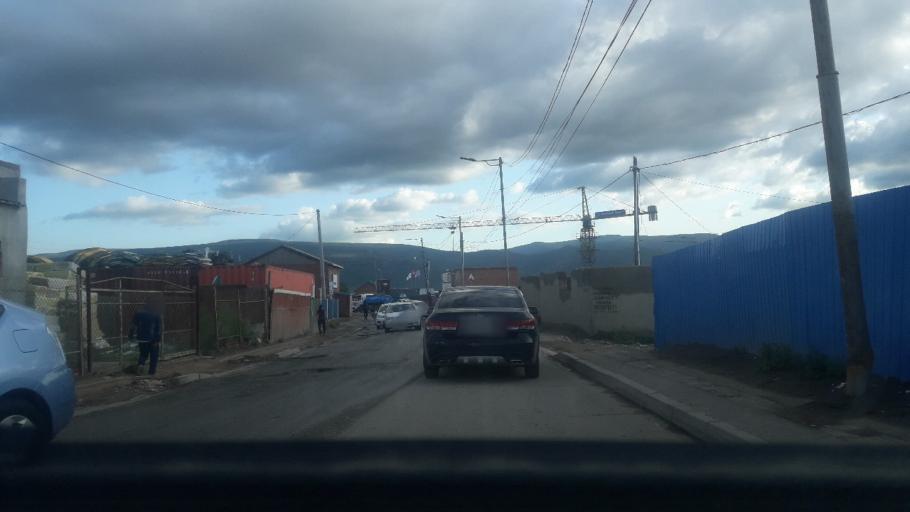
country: MN
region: Ulaanbaatar
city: Ulaanbaatar
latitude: 47.9224
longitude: 106.9955
